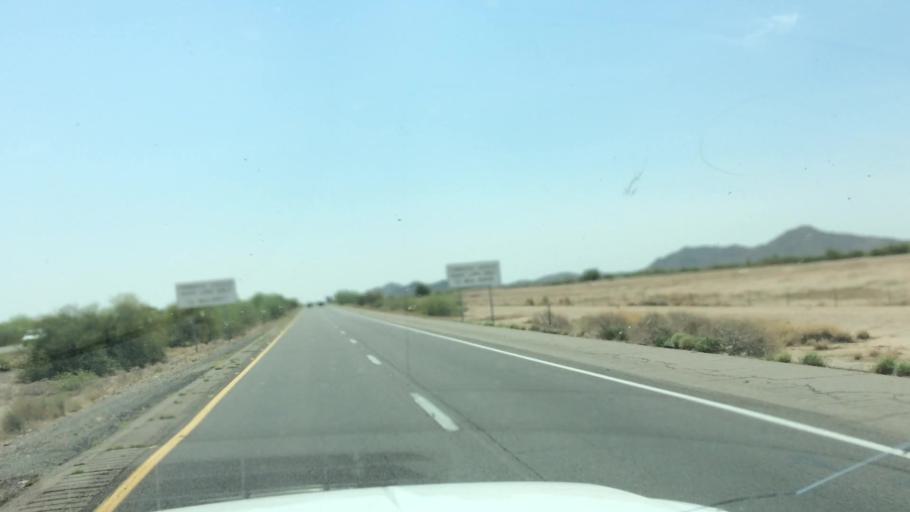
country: US
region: Arizona
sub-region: Pinal County
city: Sacaton
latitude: 33.0687
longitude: -111.8045
